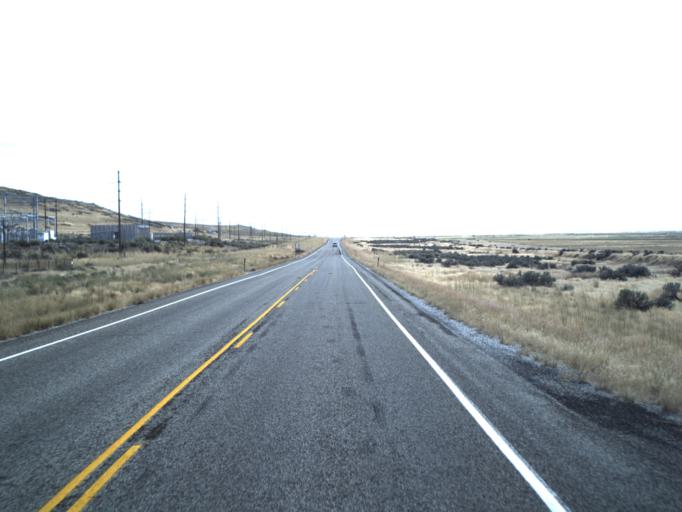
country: US
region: Utah
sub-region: Box Elder County
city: Tremonton
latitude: 41.6484
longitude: -112.4344
